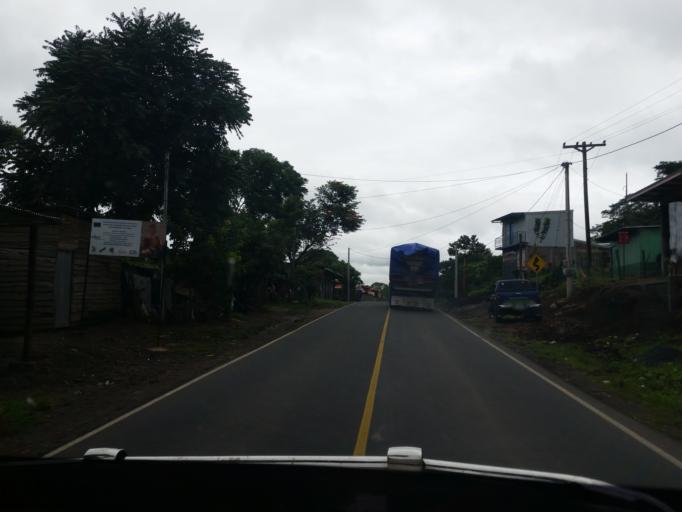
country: NI
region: Jinotega
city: Jinotega
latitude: 13.1132
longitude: -86.0061
